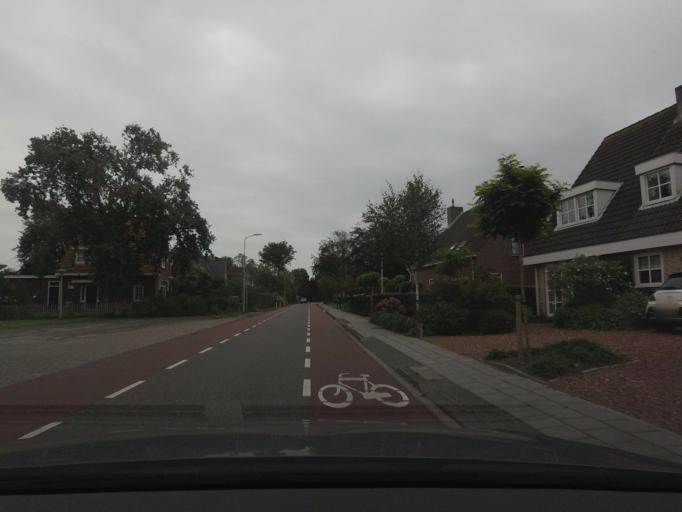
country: NL
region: North Holland
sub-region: Gemeente Schagen
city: Harenkarspel
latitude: 52.7097
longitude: 4.6892
